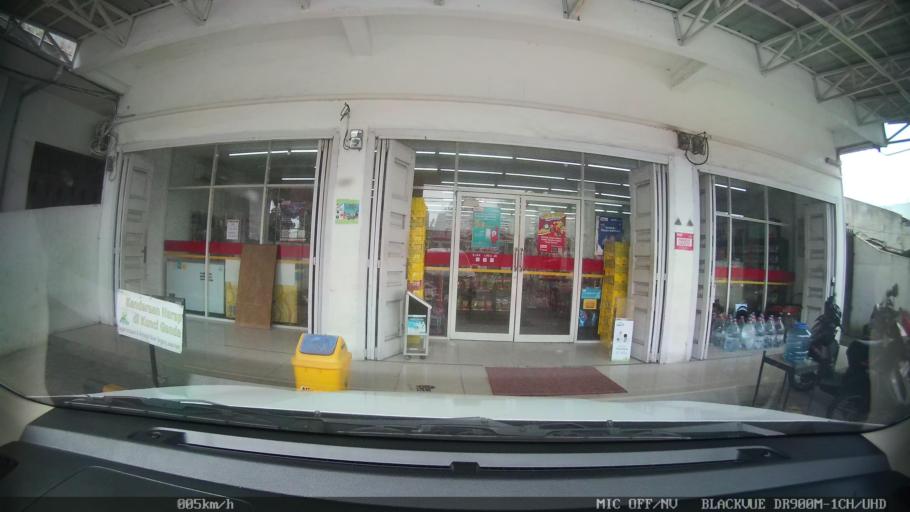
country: ID
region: North Sumatra
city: Sunggal
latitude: 3.5980
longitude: 98.6181
